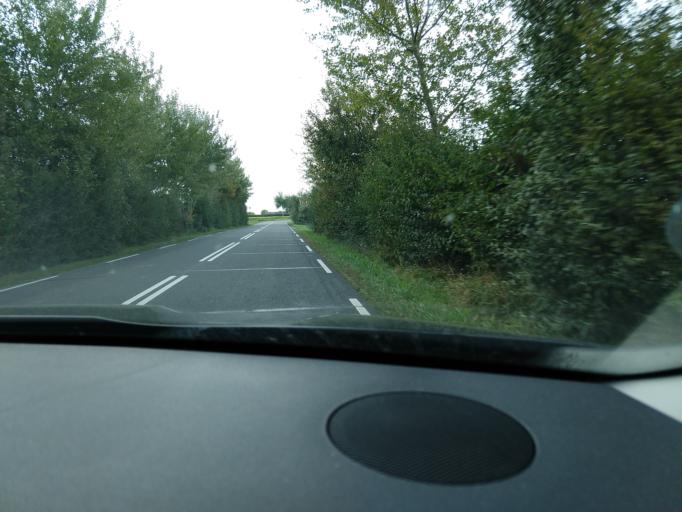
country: NL
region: Zeeland
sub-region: Gemeente Vlissingen
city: Vlissingen
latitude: 51.5155
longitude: 3.5226
